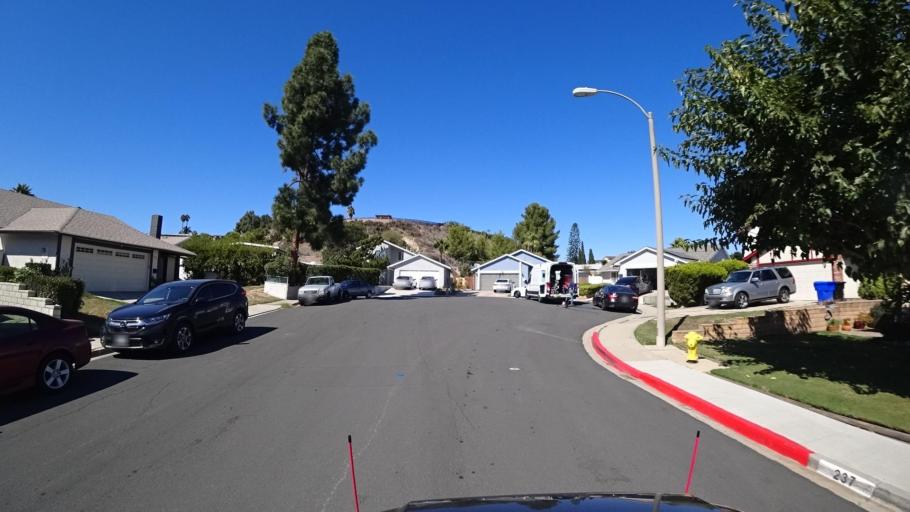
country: US
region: California
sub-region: San Diego County
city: La Presa
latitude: 32.7007
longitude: -117.0238
